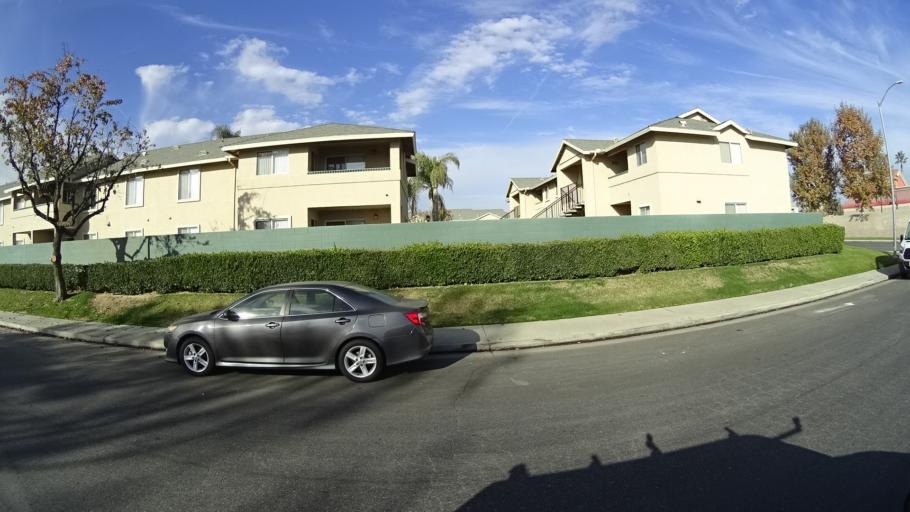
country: US
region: California
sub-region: Kern County
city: Greenacres
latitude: 35.3969
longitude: -119.1129
